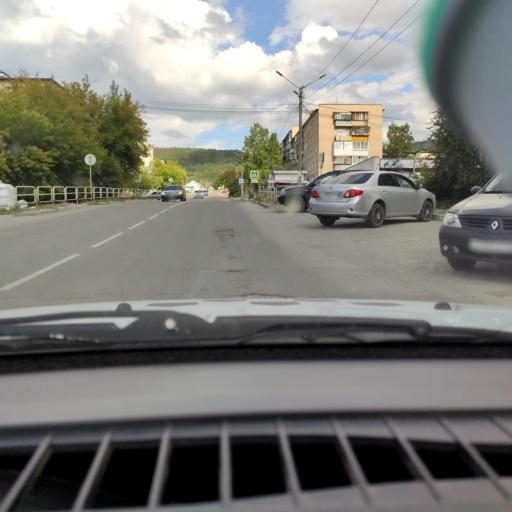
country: RU
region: Chelyabinsk
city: Miass
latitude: 55.0633
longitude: 60.1176
